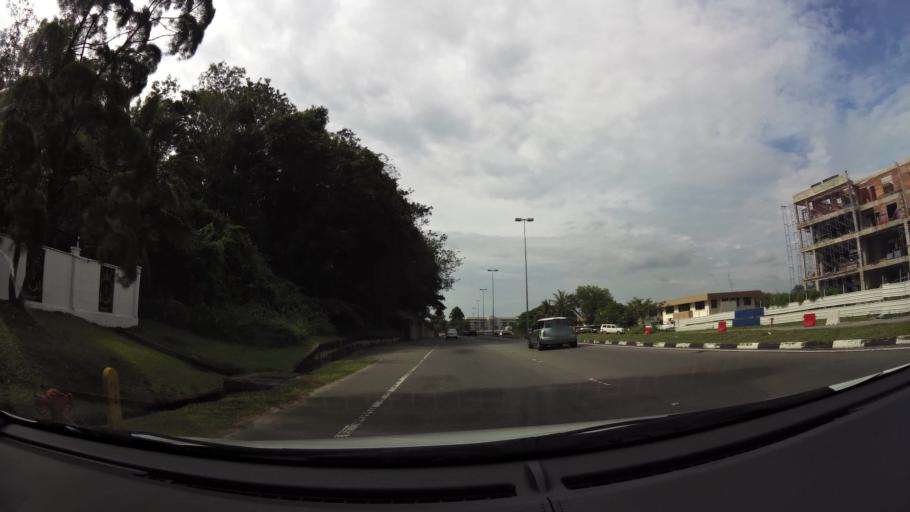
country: BN
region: Brunei and Muara
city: Bandar Seri Begawan
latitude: 4.8890
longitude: 114.8976
